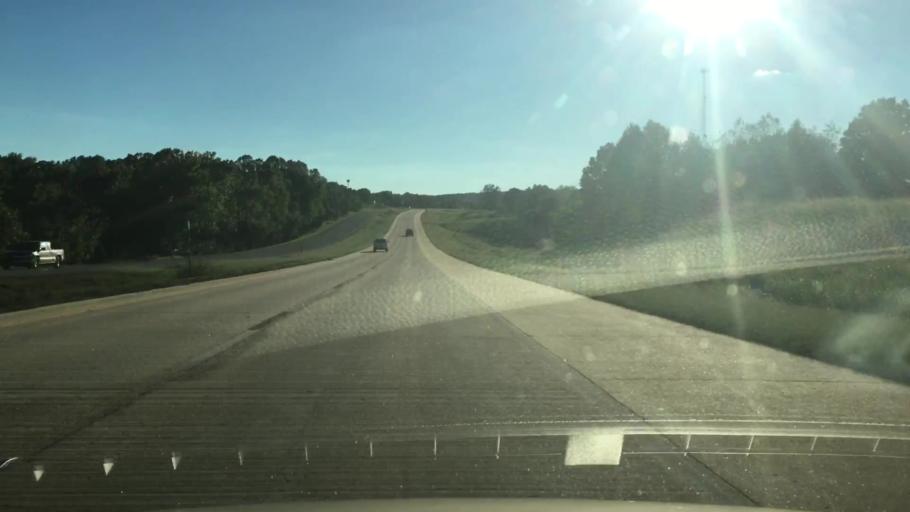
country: US
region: Oklahoma
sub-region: Cherokee County
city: Park Hill
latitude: 35.8120
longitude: -95.0670
